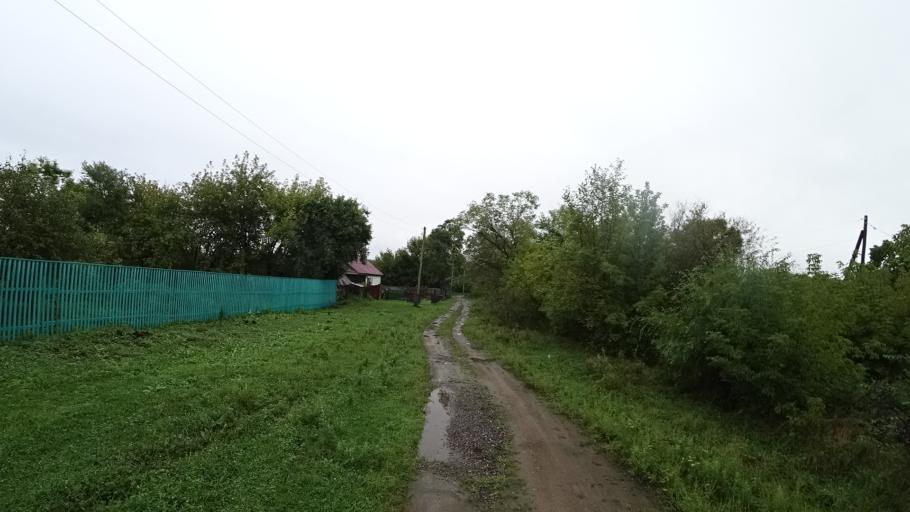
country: RU
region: Primorskiy
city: Monastyrishche
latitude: 44.2618
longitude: 132.4277
